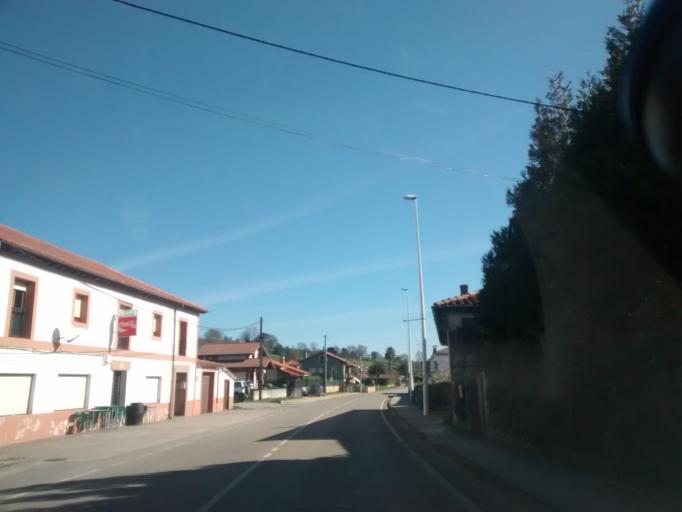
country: ES
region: Cantabria
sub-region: Provincia de Cantabria
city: Entrambasaguas
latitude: 43.3666
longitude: -3.6978
